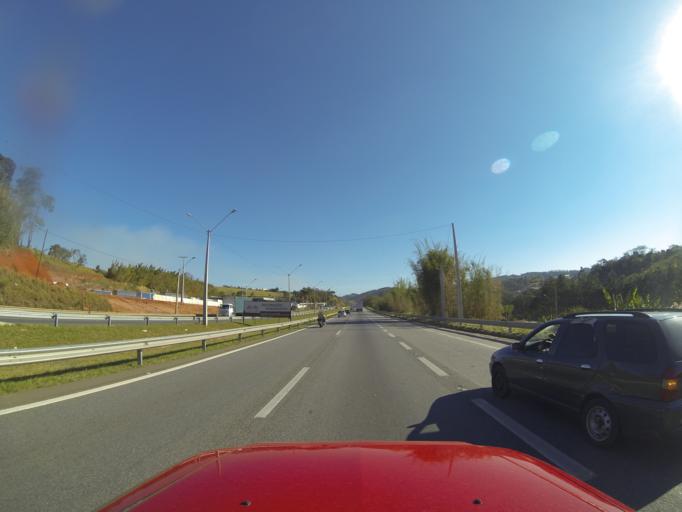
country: BR
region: Sao Paulo
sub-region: Atibaia
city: Atibaia
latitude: -23.0449
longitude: -46.5615
